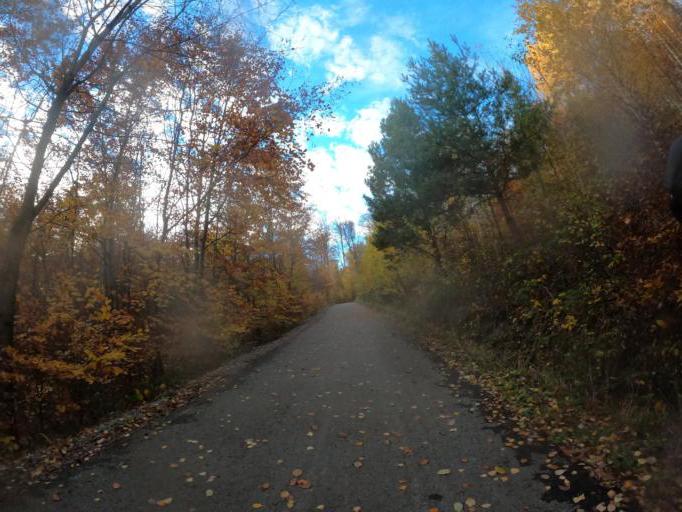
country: DE
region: Baden-Wuerttemberg
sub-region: Regierungsbezirk Stuttgart
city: Sindelfingen
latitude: 48.7181
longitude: 9.0298
